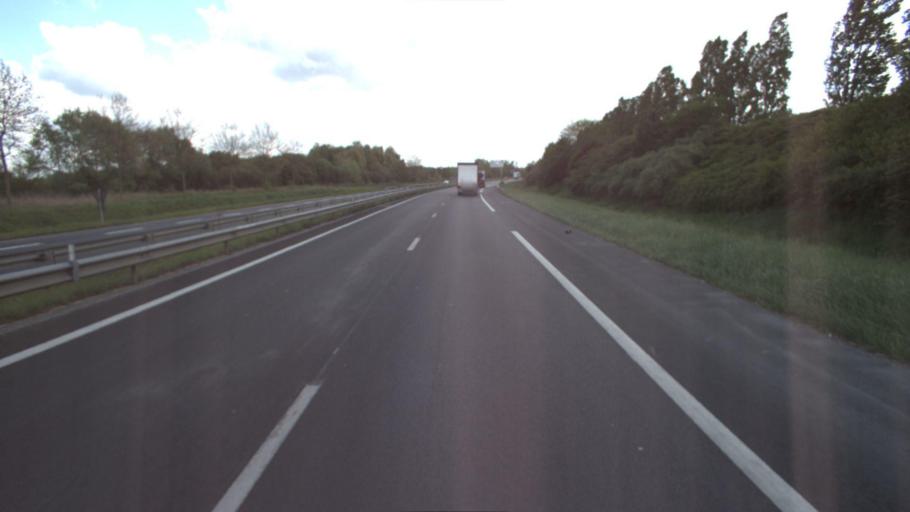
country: FR
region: Ile-de-France
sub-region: Departement de Seine-et-Marne
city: Tournan-en-Brie
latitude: 48.7287
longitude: 2.8075
